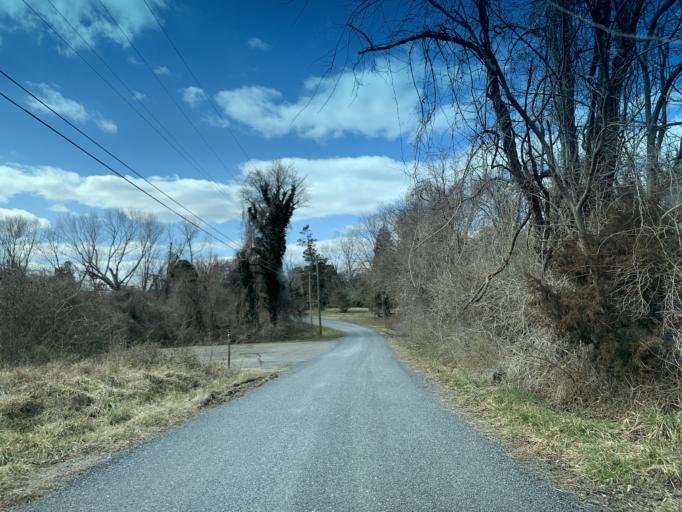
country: US
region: Maryland
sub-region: Queen Anne's County
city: Stevensville
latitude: 39.0330
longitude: -76.3079
